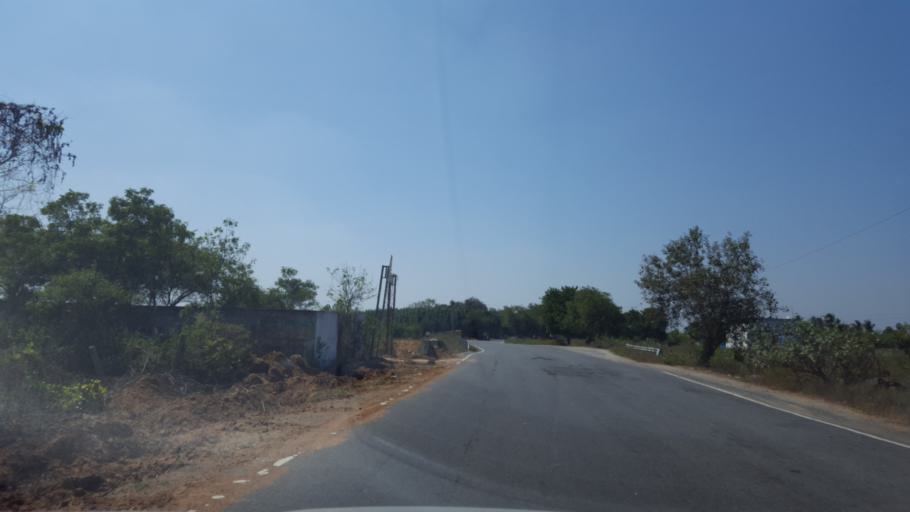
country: IN
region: Tamil Nadu
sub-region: Kancheepuram
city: Wallajahbad
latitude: 12.7741
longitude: 79.8849
